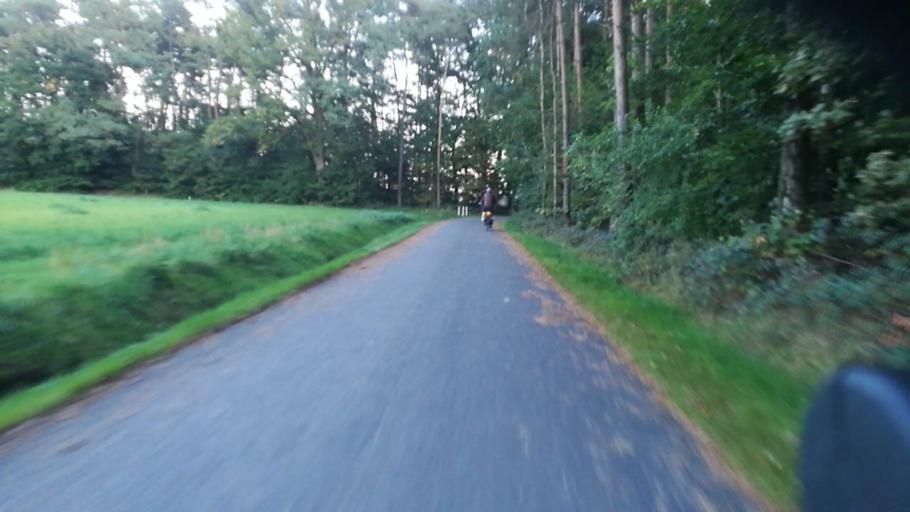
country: DE
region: North Rhine-Westphalia
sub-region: Regierungsbezirk Detmold
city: Steinhagen
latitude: 52.0149
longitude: 8.3977
